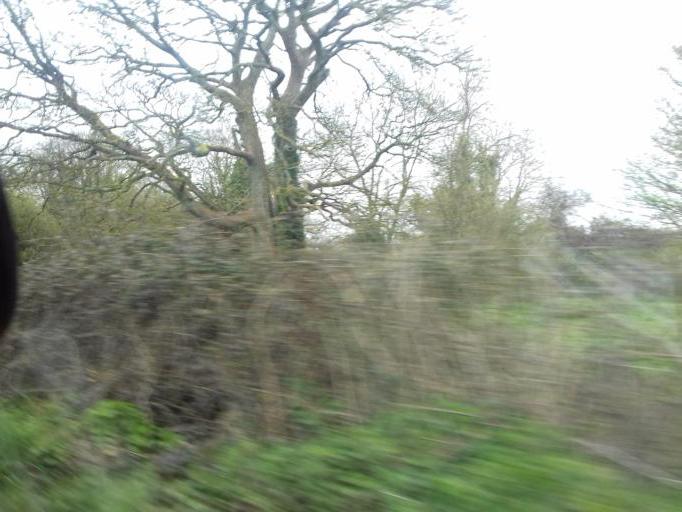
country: IE
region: Leinster
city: Donaghmede
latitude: 53.4240
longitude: -6.1665
